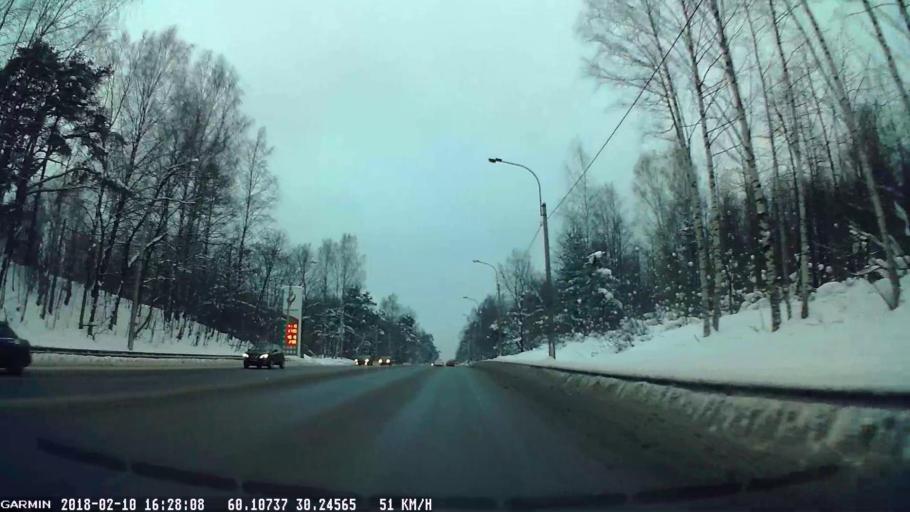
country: RU
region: St.-Petersburg
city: Levashovo
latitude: 60.1077
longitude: 30.2454
